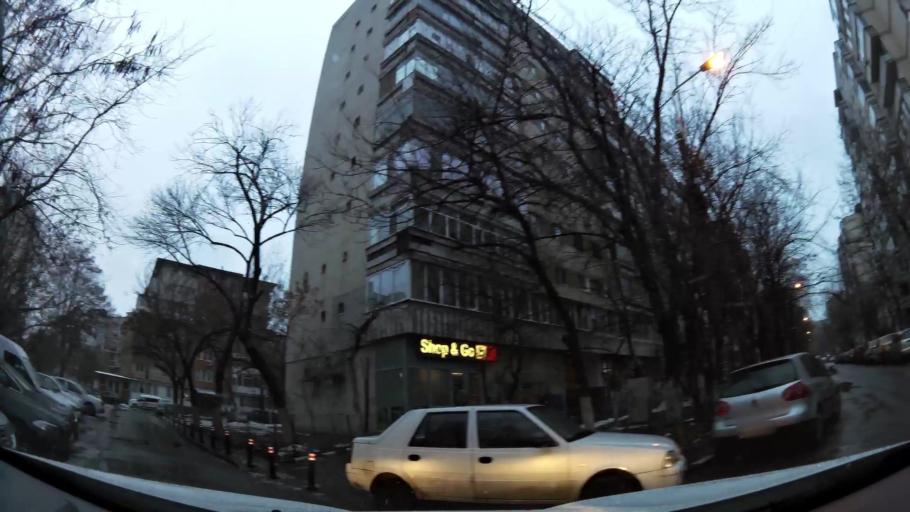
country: RO
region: Ilfov
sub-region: Comuna Chiajna
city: Rosu
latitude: 44.4319
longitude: 26.0287
